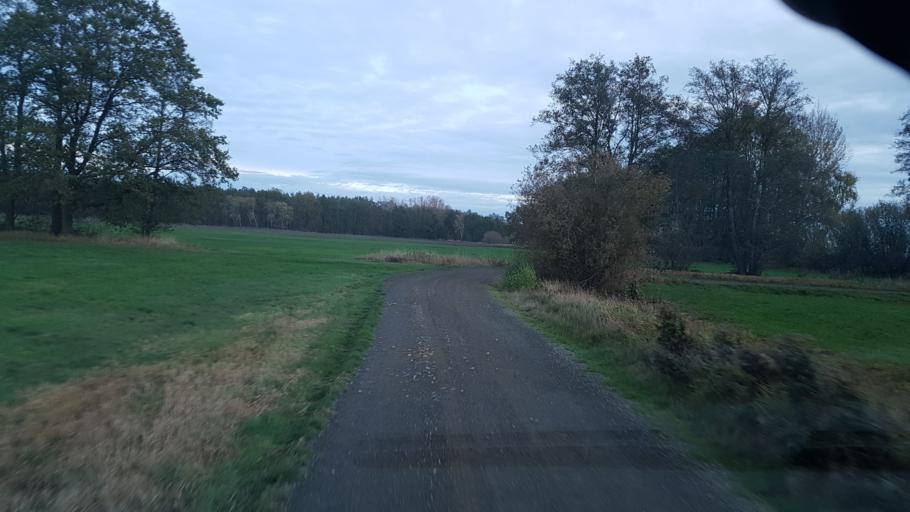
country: DE
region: Brandenburg
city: Falkenberg
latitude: 51.5315
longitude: 13.2795
